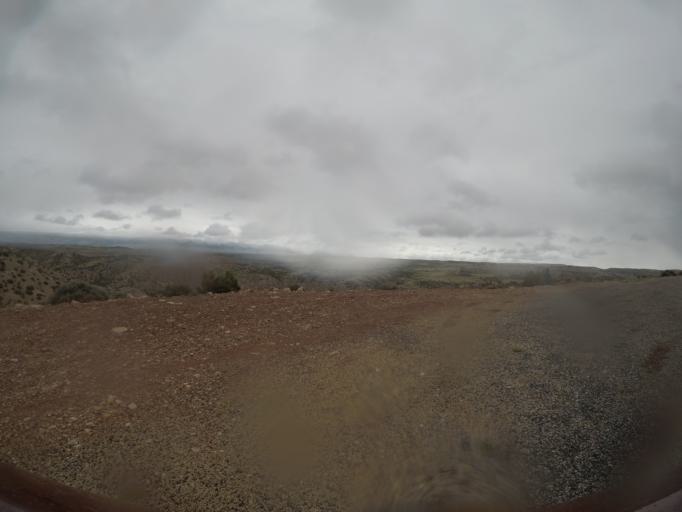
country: US
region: Wyoming
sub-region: Big Horn County
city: Lovell
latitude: 45.0433
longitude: -108.2519
